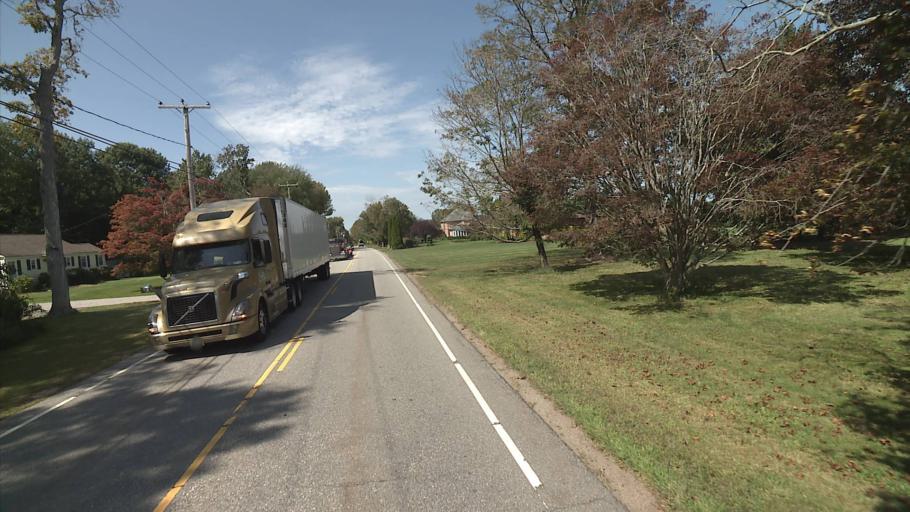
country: US
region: Connecticut
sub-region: Windham County
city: Willimantic
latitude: 41.6808
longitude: -72.2773
